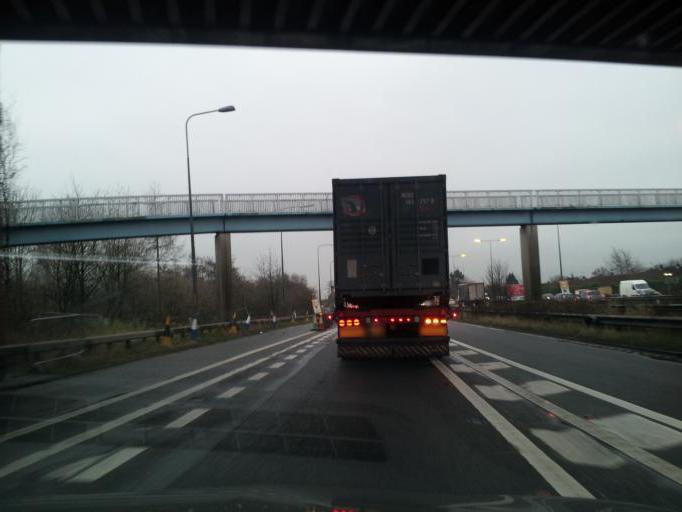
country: GB
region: England
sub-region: Manchester
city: Swinton
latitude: 53.4833
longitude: -2.3756
